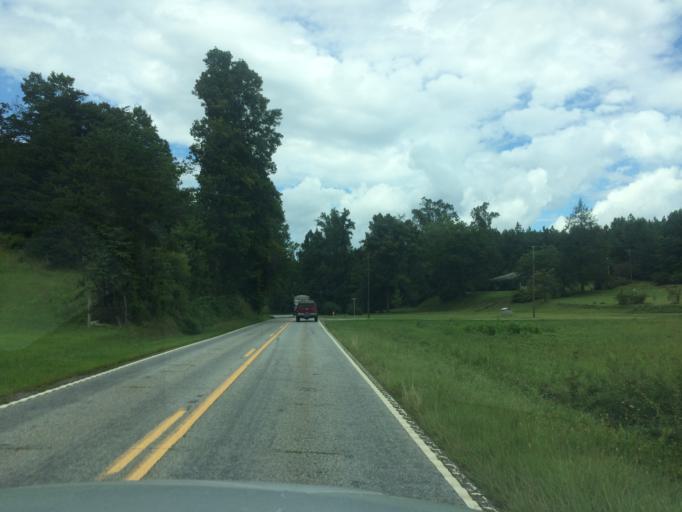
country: US
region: North Carolina
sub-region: Rutherford County
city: Lake Lure
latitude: 35.3635
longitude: -82.1817
